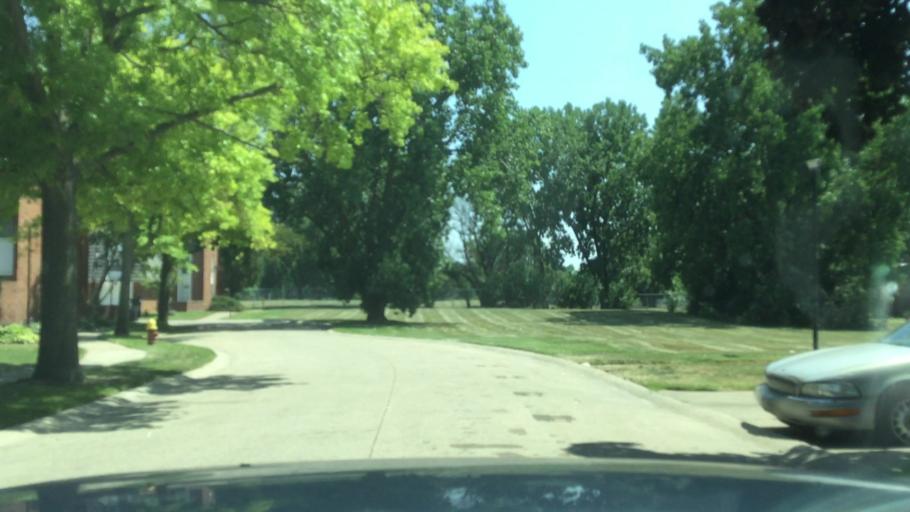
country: US
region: Michigan
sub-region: Wayne County
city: Detroit
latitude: 42.3468
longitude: -83.0302
